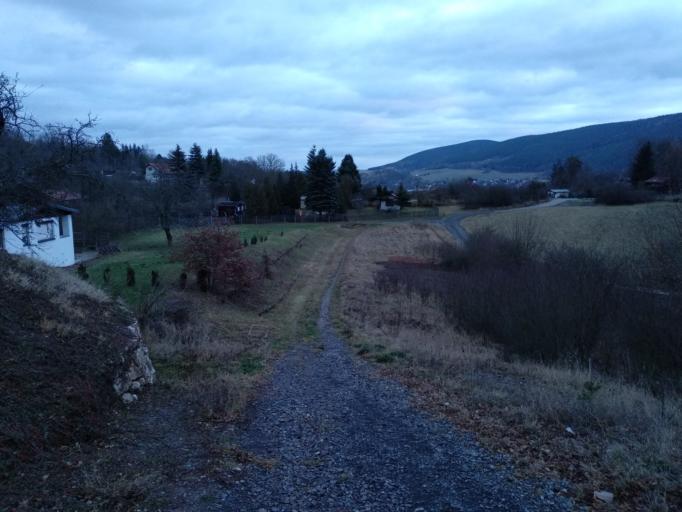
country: DE
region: Thuringia
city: Bad Blankenburg
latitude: 50.6888
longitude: 11.2568
